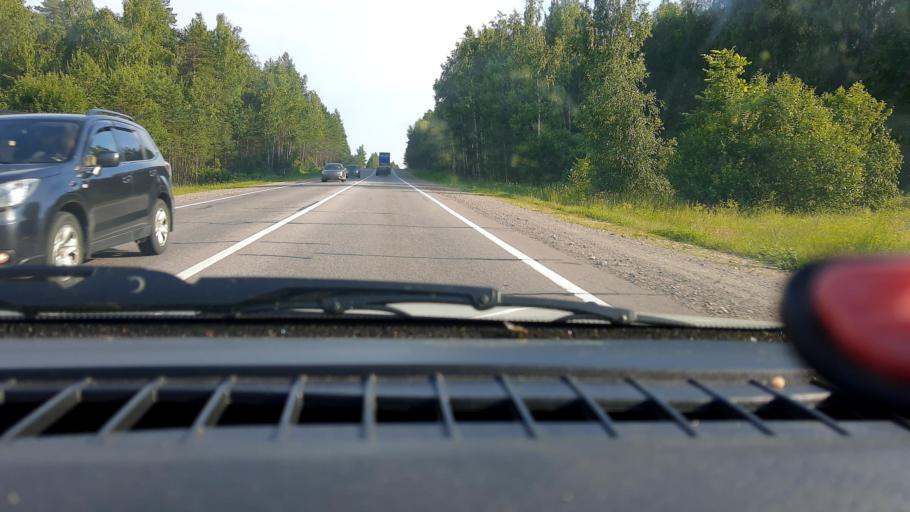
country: RU
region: Nizjnij Novgorod
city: Surovatikha
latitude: 55.6523
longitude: 43.9911
